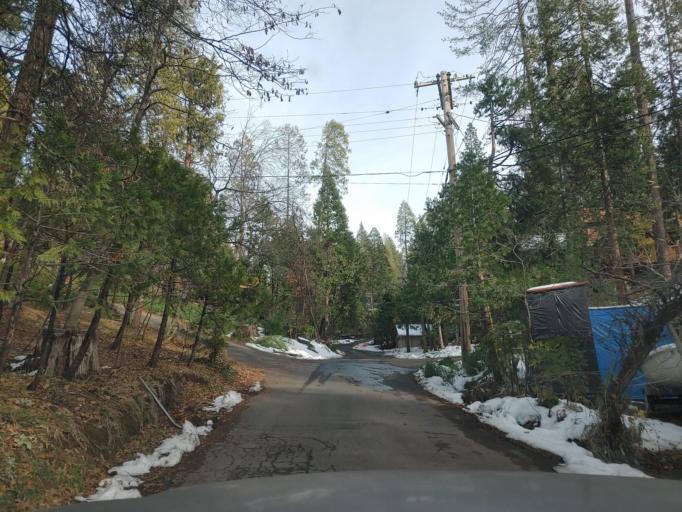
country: US
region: California
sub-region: Tuolumne County
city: Twain Harte
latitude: 38.0352
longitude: -120.2309
